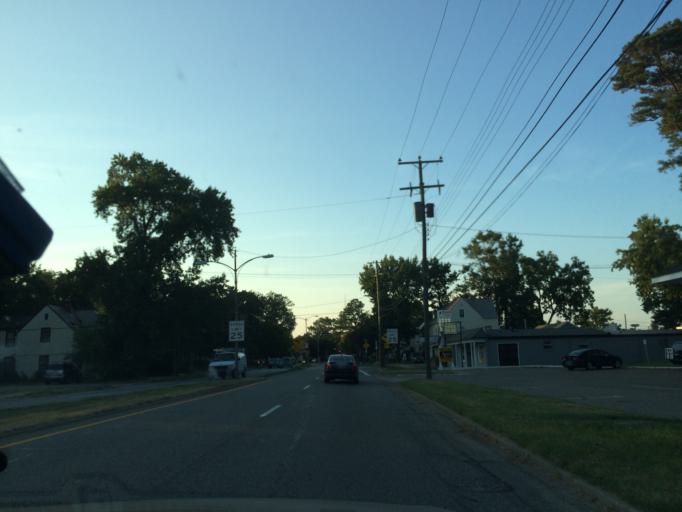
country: US
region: Virginia
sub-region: City of Newport News
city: Newport News
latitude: 37.0298
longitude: -76.4577
